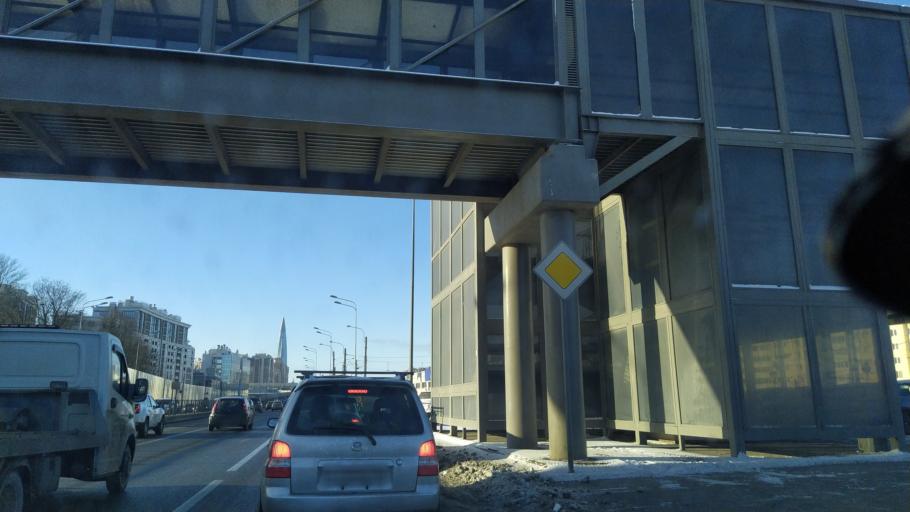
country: RU
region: St.-Petersburg
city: Staraya Derevnya
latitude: 59.9838
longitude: 30.2435
